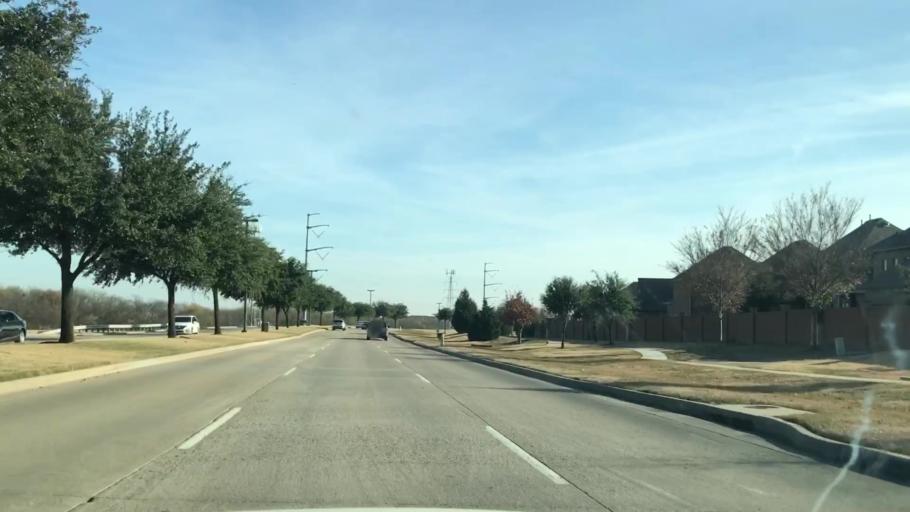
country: US
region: Texas
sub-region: Dallas County
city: Farmers Branch
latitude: 32.9072
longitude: -96.9444
